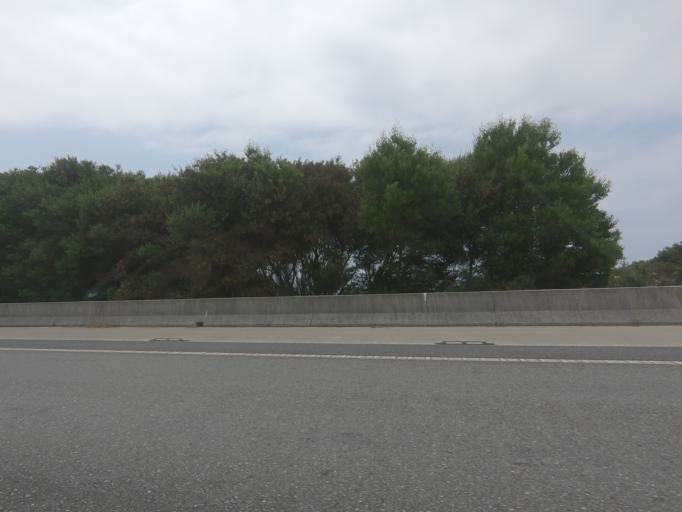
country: ES
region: Galicia
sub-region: Provincia de Pontevedra
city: Oia
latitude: 41.9814
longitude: -8.8846
